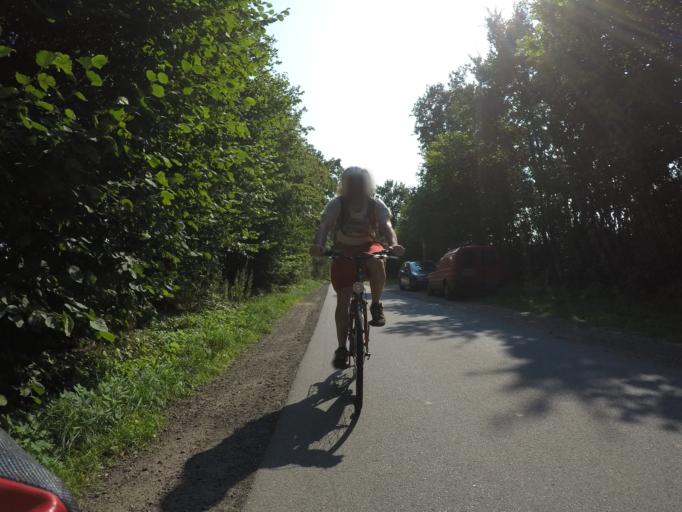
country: DE
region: Schleswig-Holstein
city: Todesfelde
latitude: 53.8871
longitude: 10.1740
